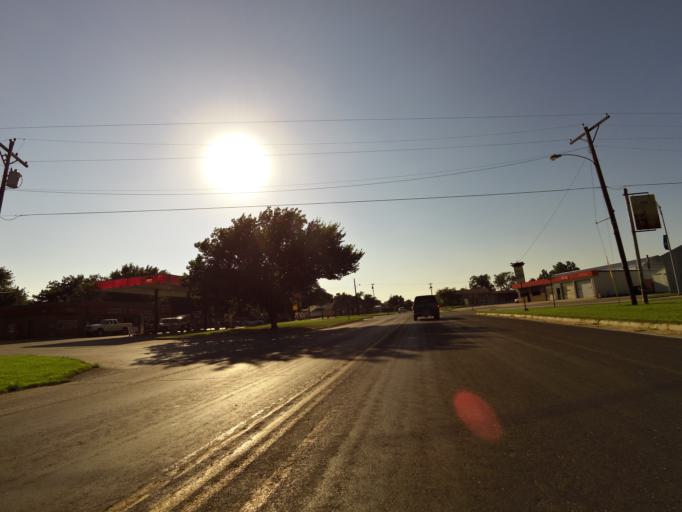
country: US
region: Kansas
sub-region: Harvey County
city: Hesston
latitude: 38.1372
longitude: -97.4293
